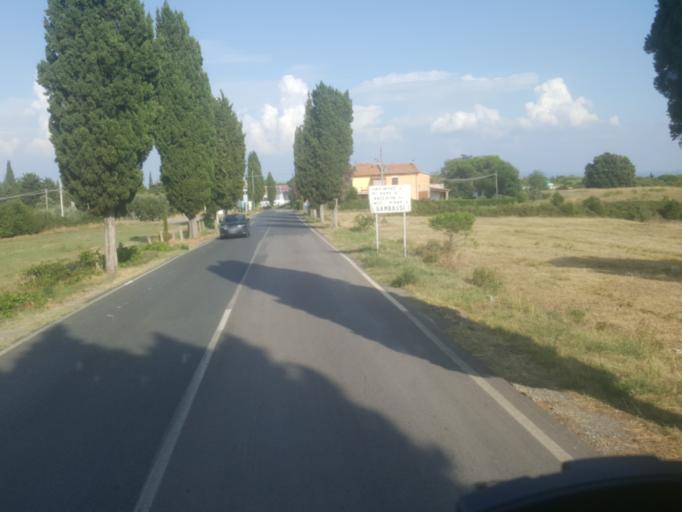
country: IT
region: Tuscany
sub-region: Province of Florence
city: Gambassi Terme
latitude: 43.5328
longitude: 10.9427
